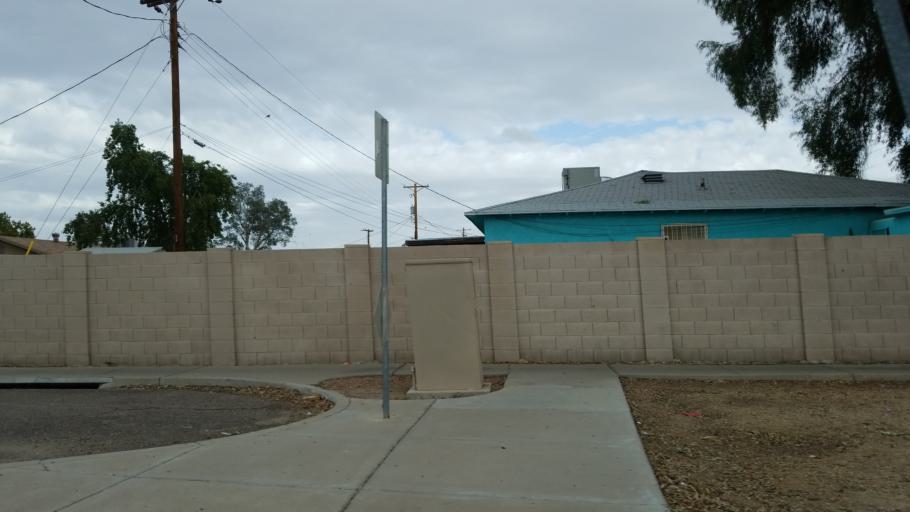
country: US
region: Arizona
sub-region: Maricopa County
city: Glendale
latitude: 33.5026
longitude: -112.1863
